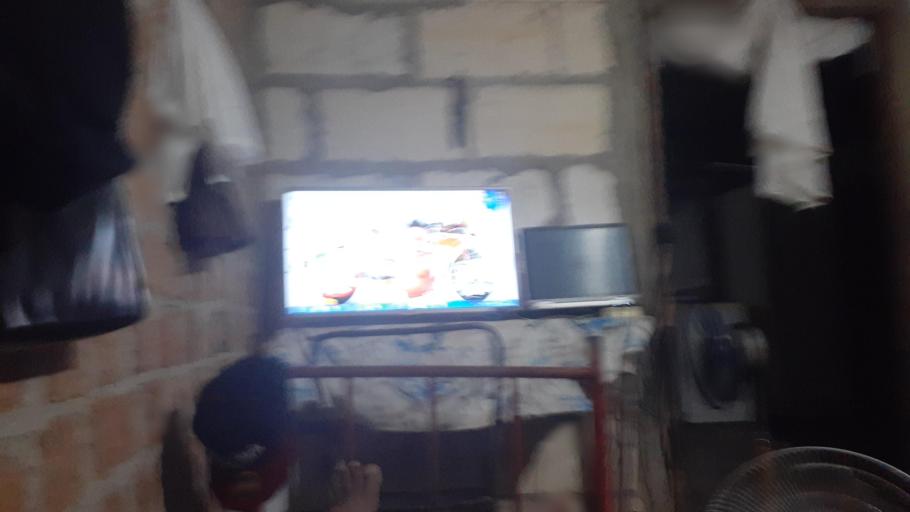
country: CU
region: La Habana
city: Alamar
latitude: 23.1531
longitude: -82.1514
